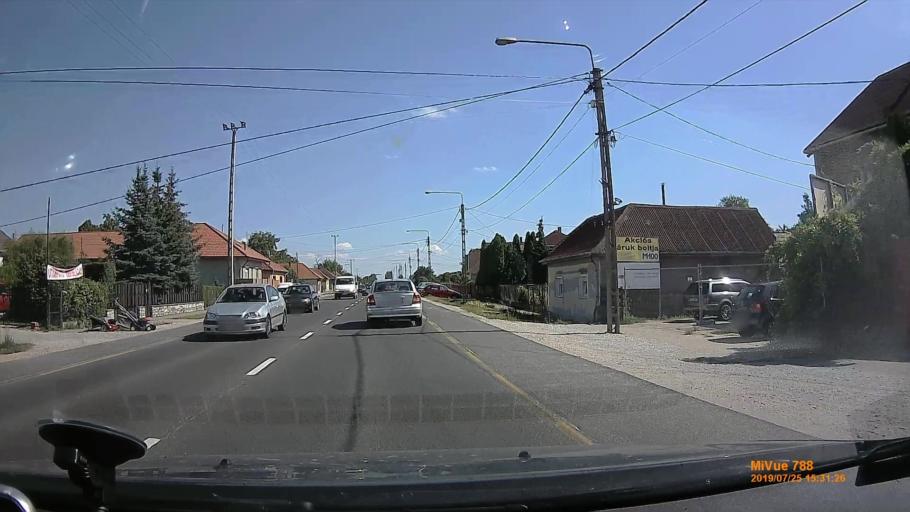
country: HU
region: Borsod-Abauj-Zemplen
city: Malyi
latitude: 48.0126
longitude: 20.8248
